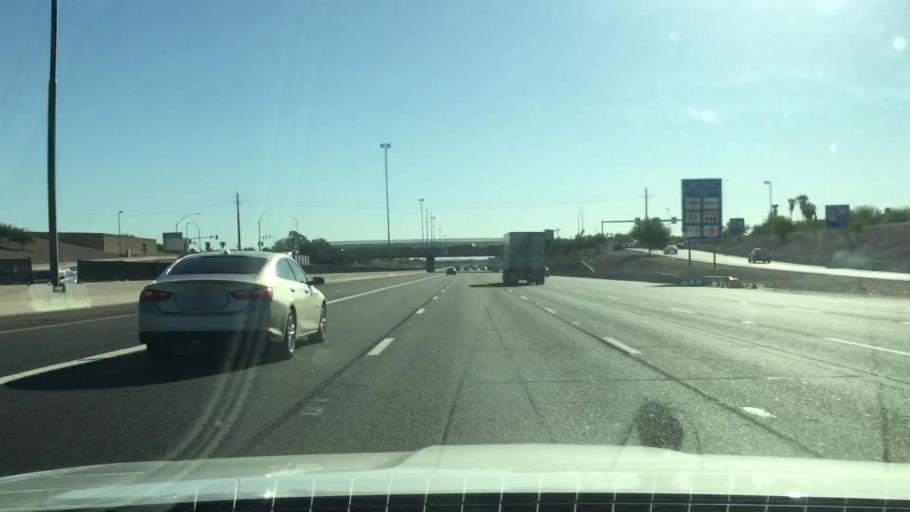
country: US
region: Arizona
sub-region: Maricopa County
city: Gilbert
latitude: 33.3854
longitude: -111.8086
